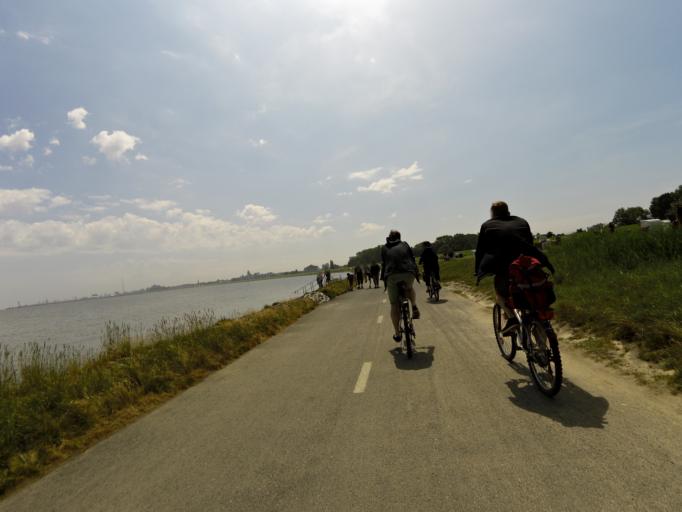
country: DE
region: Lower Saxony
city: Cuxhaven
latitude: 53.8881
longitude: 8.6832
